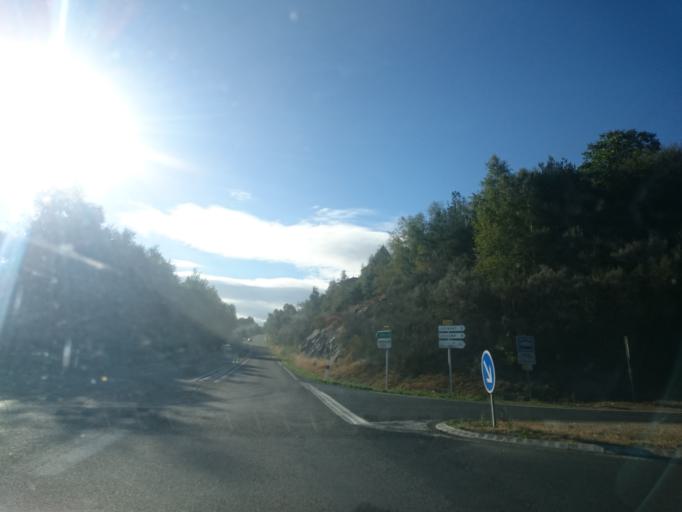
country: FR
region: Midi-Pyrenees
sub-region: Departement de l'Aveyron
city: Entraygues-sur-Truyere
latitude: 44.7464
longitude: 2.4879
